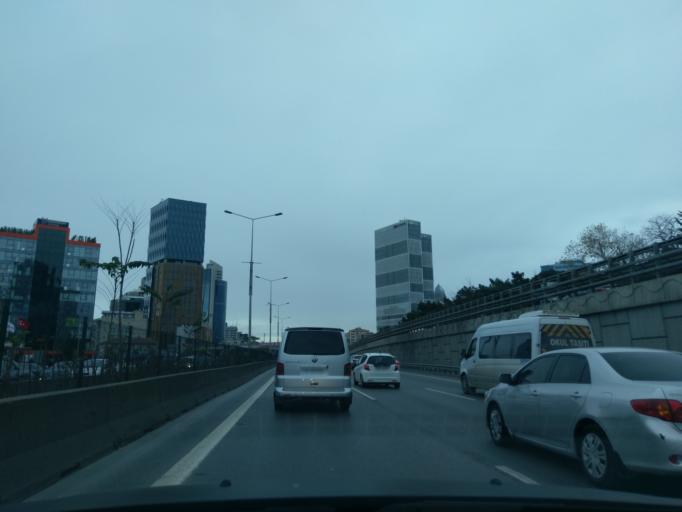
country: TR
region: Istanbul
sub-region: Atasehir
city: Atasehir
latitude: 40.9689
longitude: 29.1027
